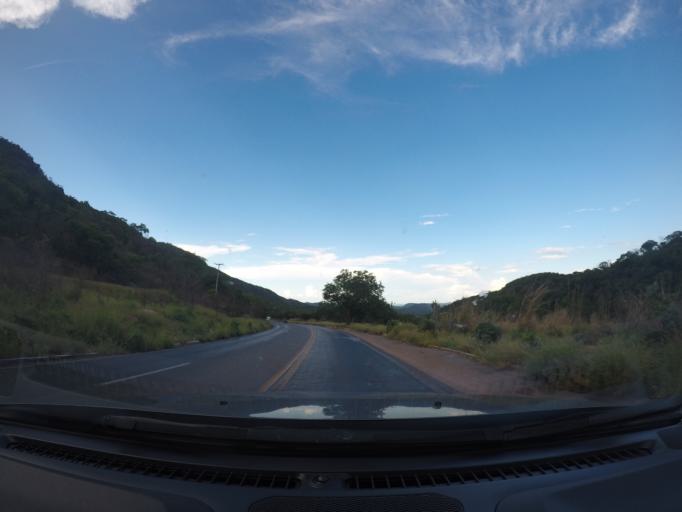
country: BR
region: Bahia
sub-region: Ibotirama
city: Ibotirama
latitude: -12.1390
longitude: -43.3514
